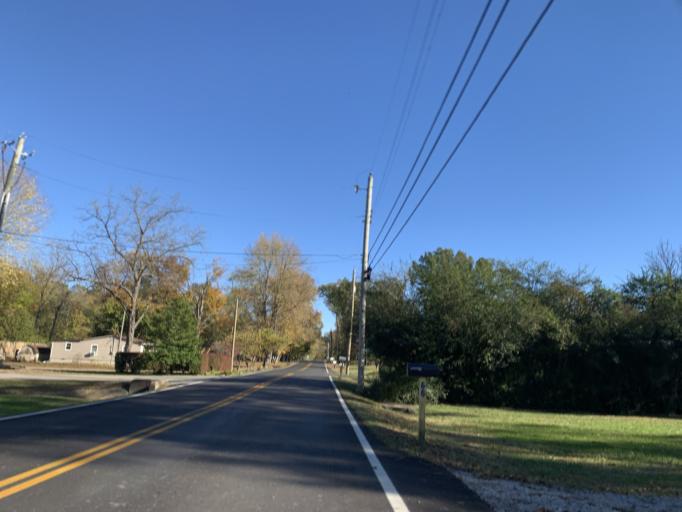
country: US
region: Kentucky
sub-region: Jefferson County
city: Pleasure Ridge Park
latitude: 38.1573
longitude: -85.8747
